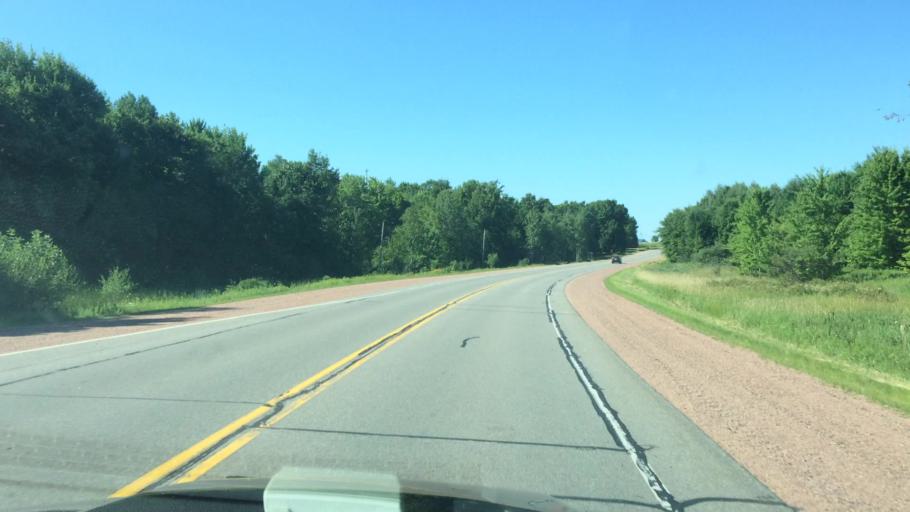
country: US
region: Wisconsin
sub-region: Marathon County
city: Stratford
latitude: 44.7355
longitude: -90.0804
